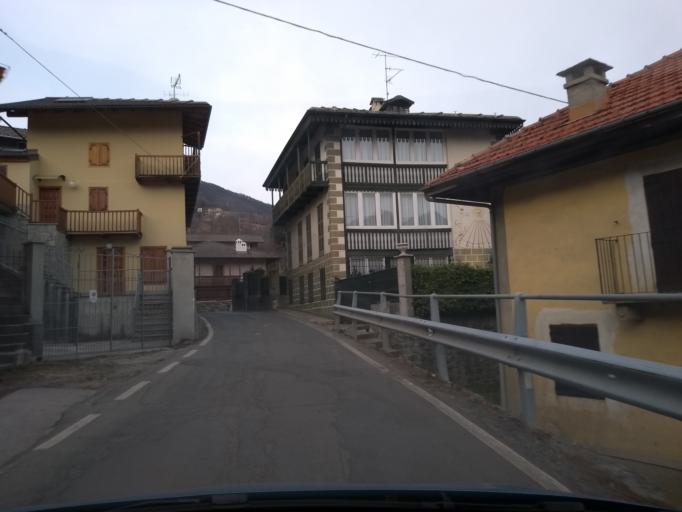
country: IT
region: Piedmont
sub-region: Provincia di Torino
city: Viu
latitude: 45.2343
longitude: 7.3718
